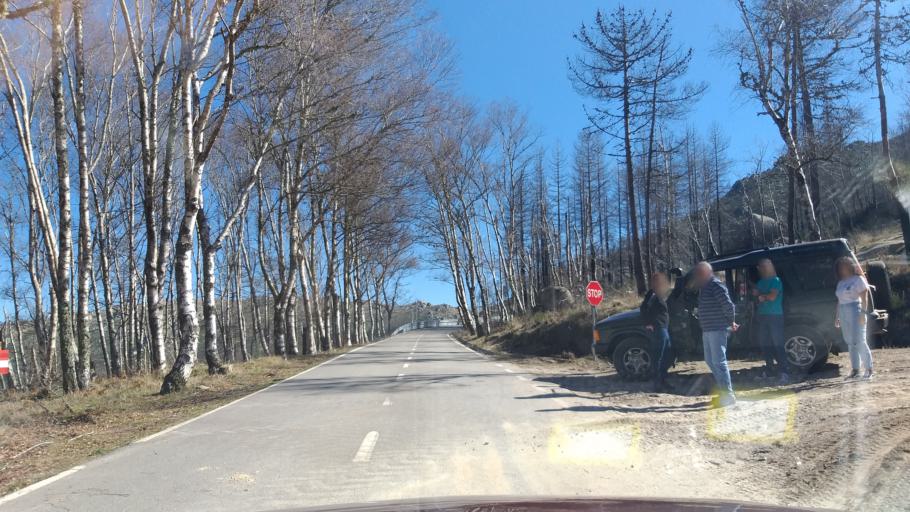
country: PT
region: Guarda
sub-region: Manteigas
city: Manteigas
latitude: 40.4875
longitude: -7.5224
